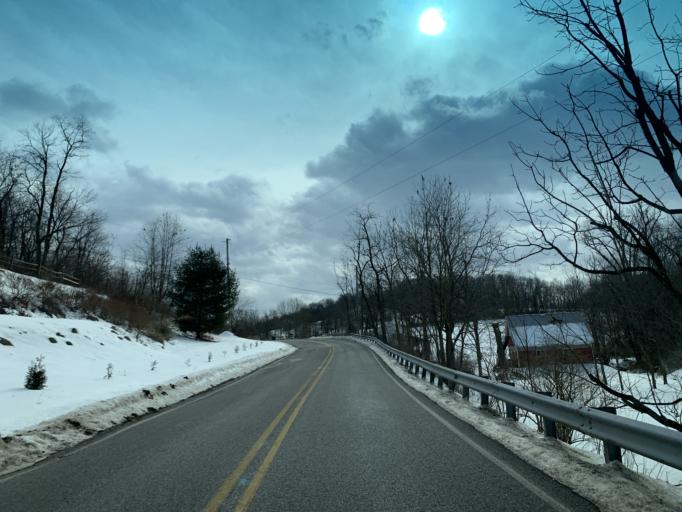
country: US
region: Pennsylvania
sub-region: York County
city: Shrewsbury
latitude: 39.7967
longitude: -76.6529
